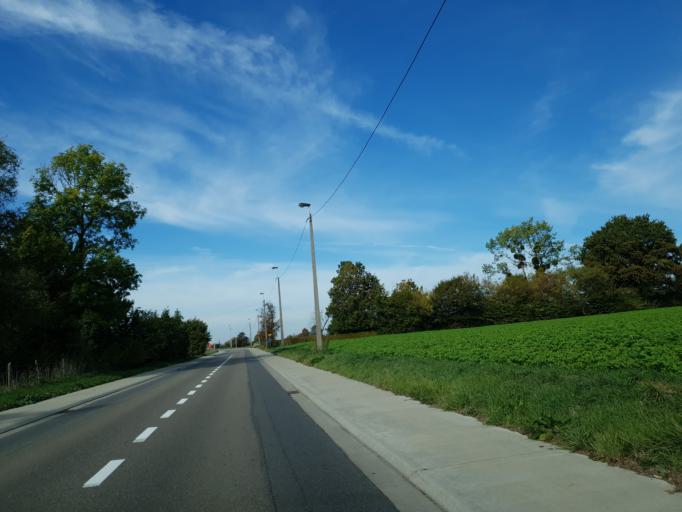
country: BE
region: Flanders
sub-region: Provincie Vlaams-Brabant
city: Kortenberg
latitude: 50.8888
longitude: 4.5740
